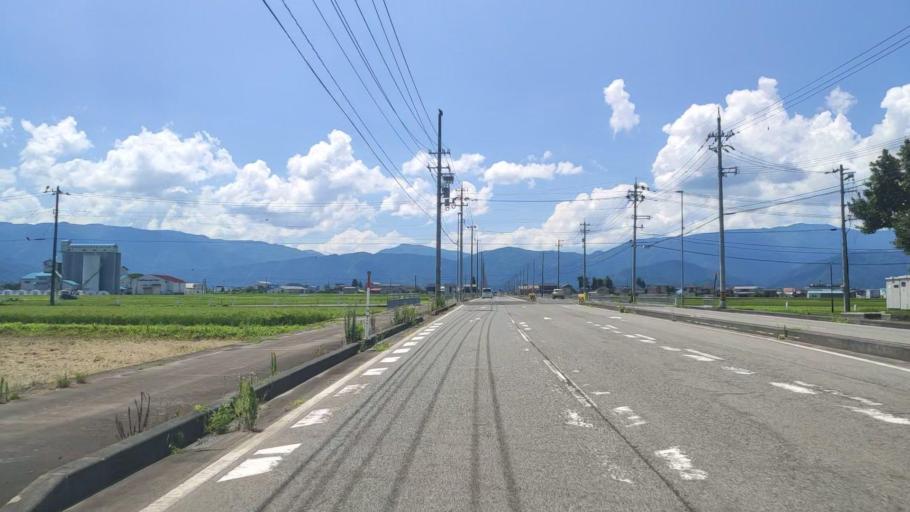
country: JP
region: Fukui
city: Ono
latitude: 35.9945
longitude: 136.5095
